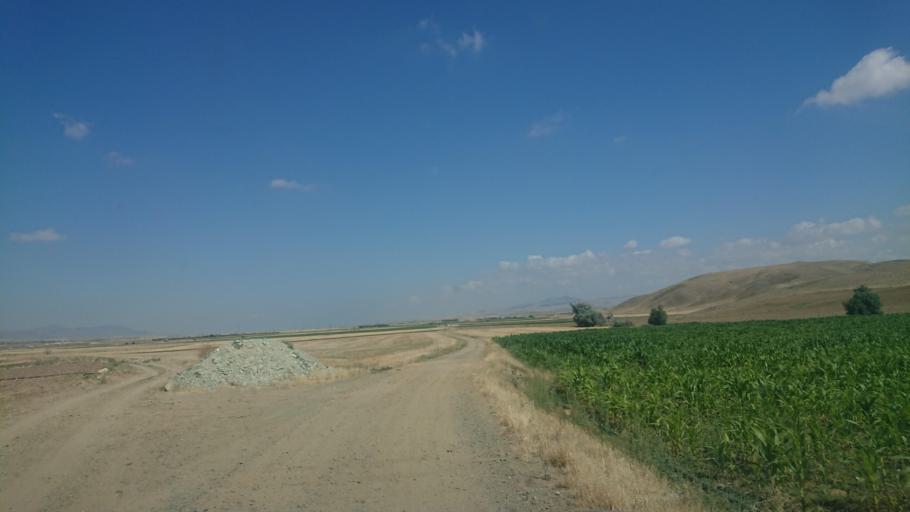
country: TR
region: Aksaray
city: Sariyahsi
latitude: 38.9695
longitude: 33.9193
